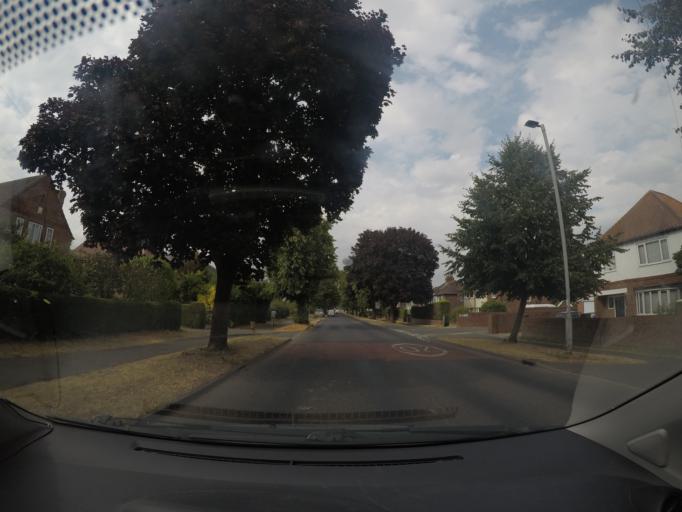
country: GB
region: England
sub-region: City of York
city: Nether Poppleton
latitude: 53.9588
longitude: -1.1352
